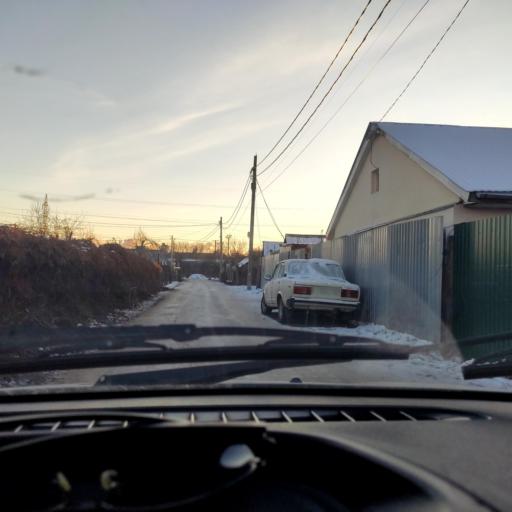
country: RU
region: Samara
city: Tol'yatti
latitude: 53.5420
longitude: 49.4386
